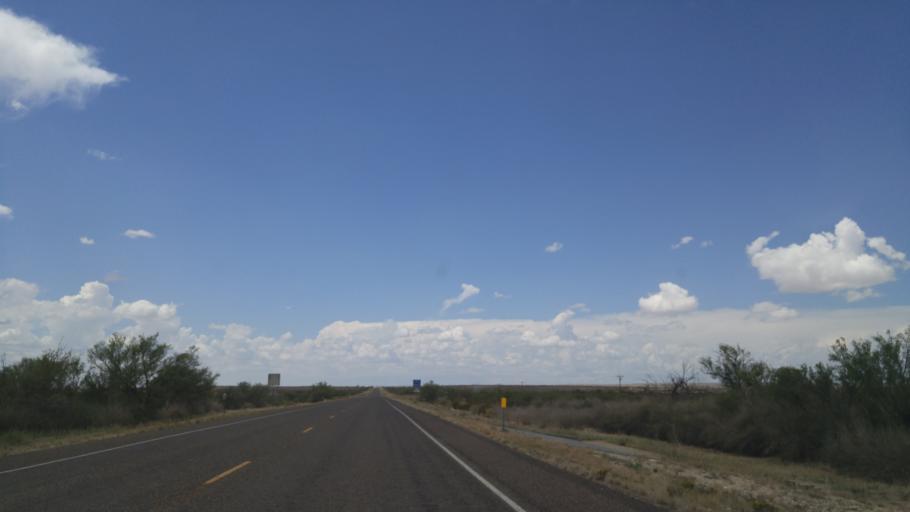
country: US
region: Texas
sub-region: Brewster County
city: Alpine
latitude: 29.6051
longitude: -103.5633
